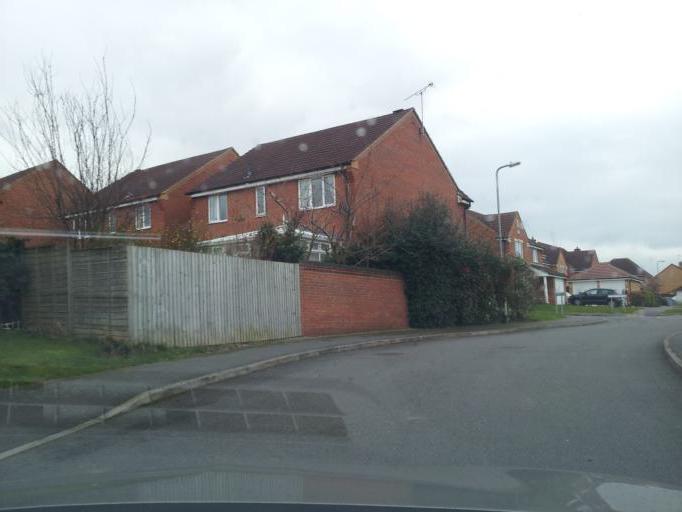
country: GB
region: England
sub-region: Lincolnshire
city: Grantham
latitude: 52.9181
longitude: -0.6565
